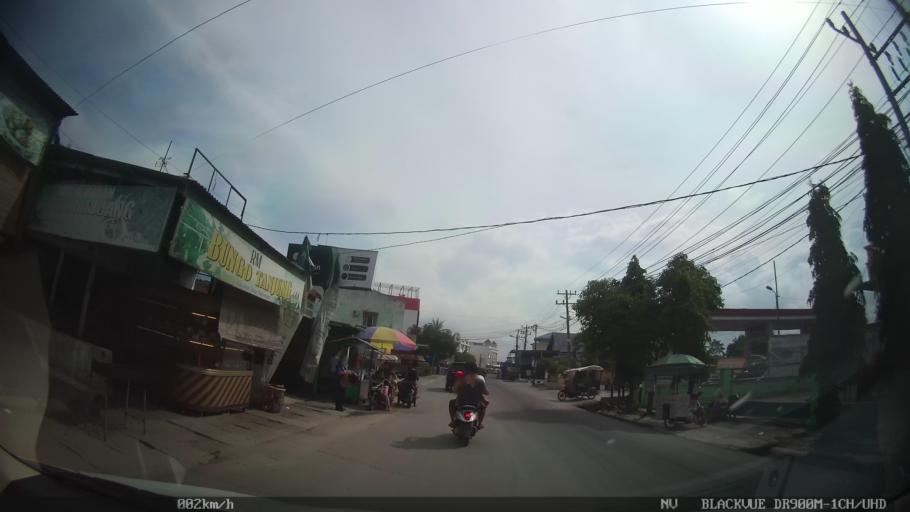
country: ID
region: North Sumatra
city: Percut
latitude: 3.6123
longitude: 98.7999
